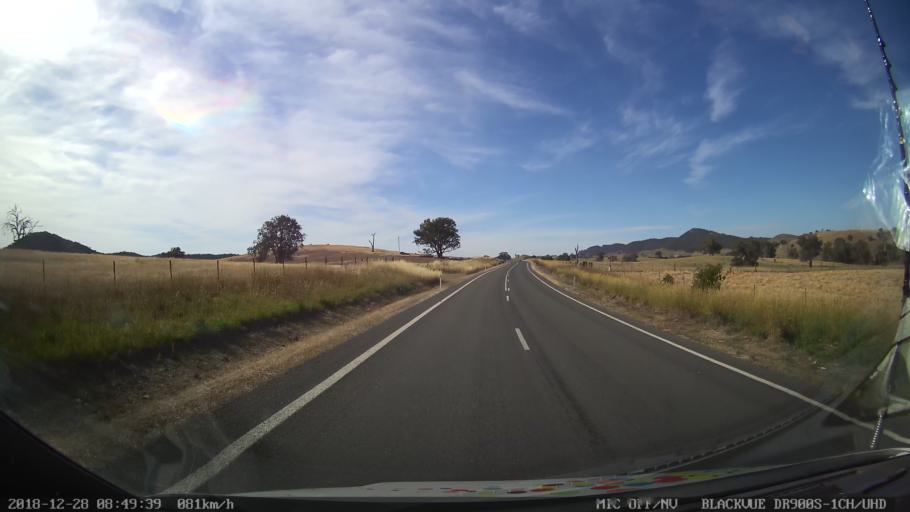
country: AU
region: New South Wales
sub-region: Upper Lachlan Shire
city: Crookwell
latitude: -34.0479
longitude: 149.3376
